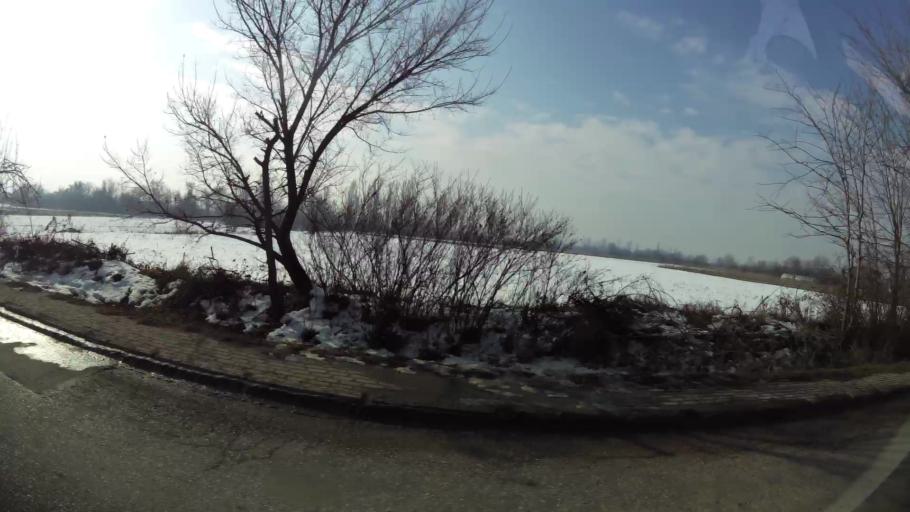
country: MK
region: Suto Orizari
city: Suto Orizare
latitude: 42.0218
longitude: 21.3865
